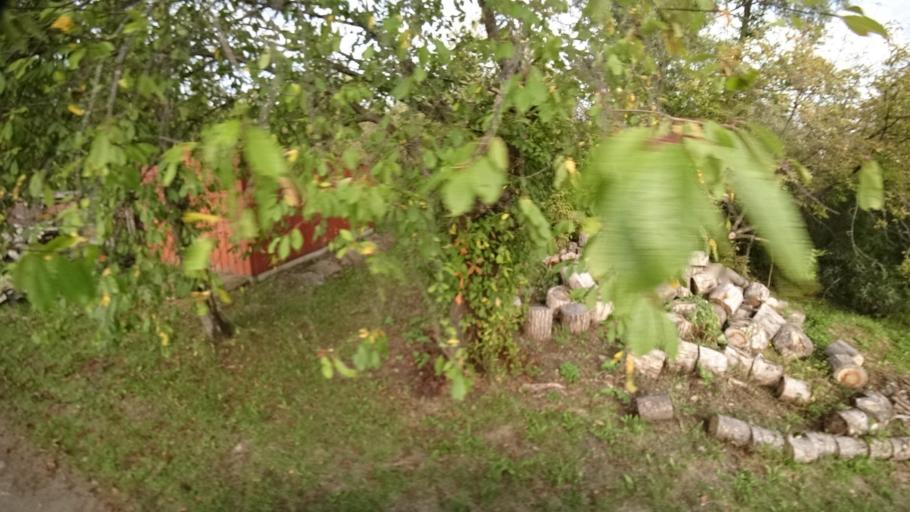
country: RU
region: Primorskiy
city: Dostoyevka
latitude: 44.2898
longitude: 133.4305
